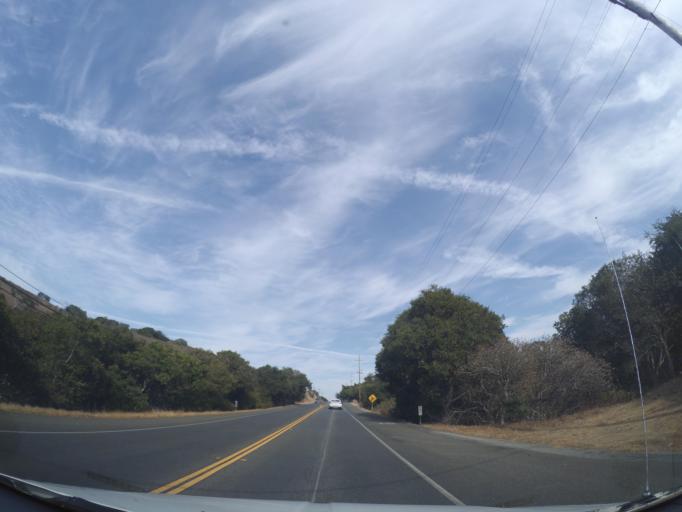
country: US
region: California
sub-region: Monterey County
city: Carmel Valley Village
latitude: 36.5699
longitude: -121.7516
